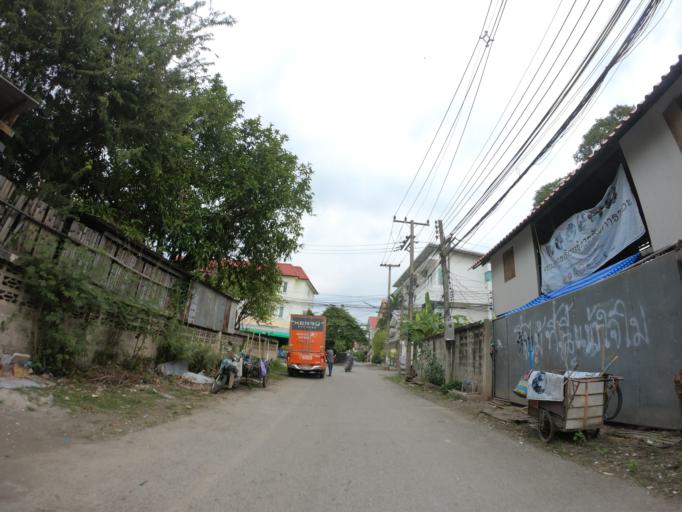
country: TH
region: Chiang Mai
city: Chiang Mai
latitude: 18.7745
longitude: 98.9916
